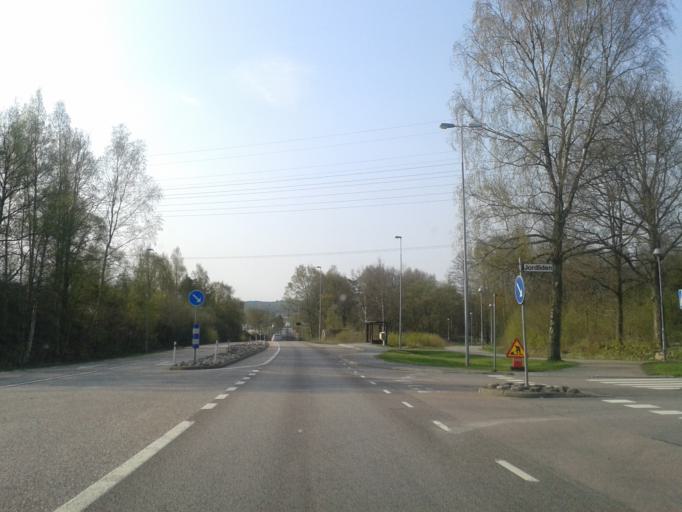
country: SE
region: Vaestra Goetaland
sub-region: Kungalvs Kommun
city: Kungalv
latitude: 57.8826
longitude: 11.9712
